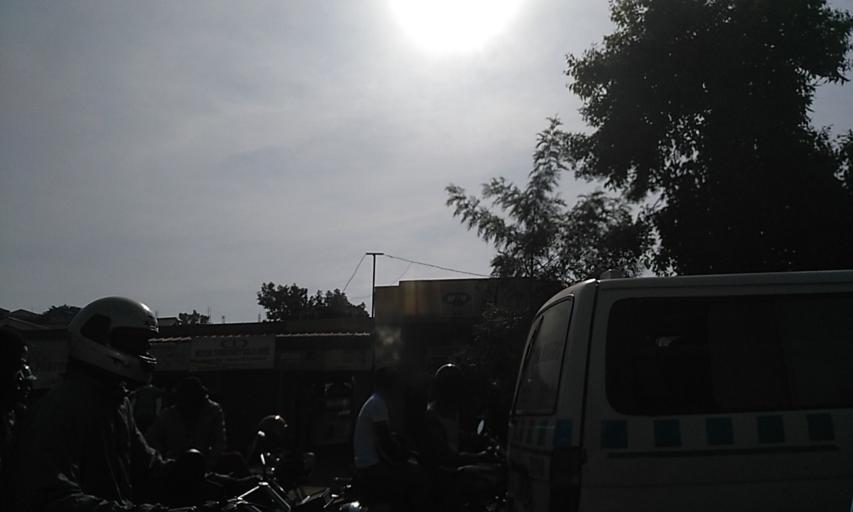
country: UG
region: Central Region
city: Kampala Central Division
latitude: 0.3680
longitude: 32.5763
